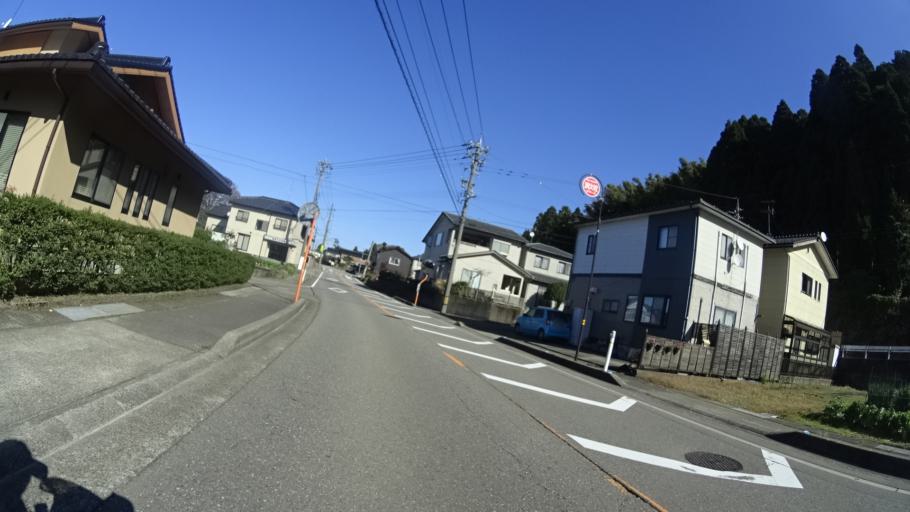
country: JP
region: Ishikawa
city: Nonoichi
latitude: 36.4969
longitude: 136.6213
